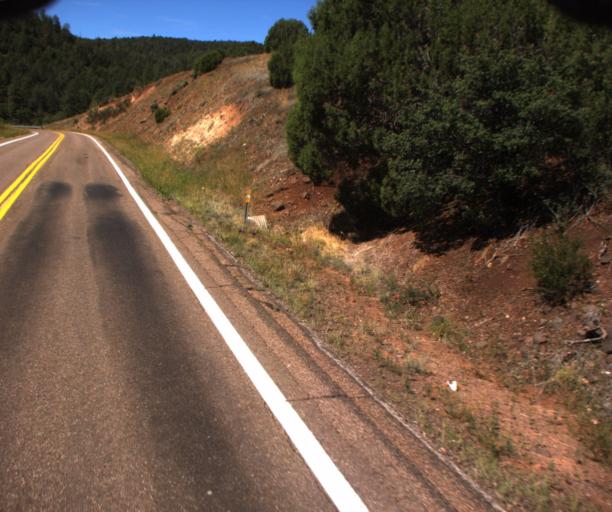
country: US
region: Arizona
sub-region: Navajo County
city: Cibecue
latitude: 33.9195
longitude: -110.3629
